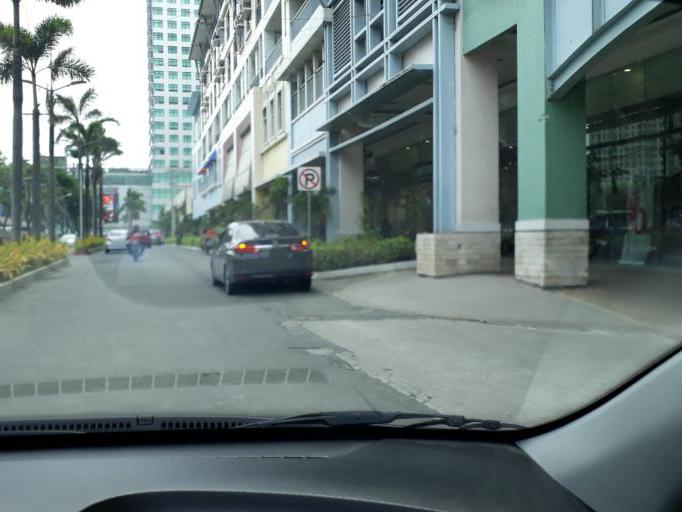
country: PH
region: Metro Manila
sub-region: Quezon City
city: Quezon City
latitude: 14.6228
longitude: 121.0555
